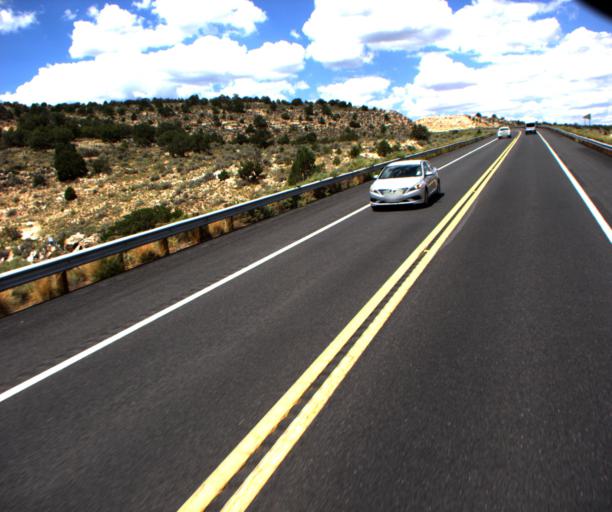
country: US
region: Arizona
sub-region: Coconino County
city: Grand Canyon
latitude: 35.9380
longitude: -111.6962
